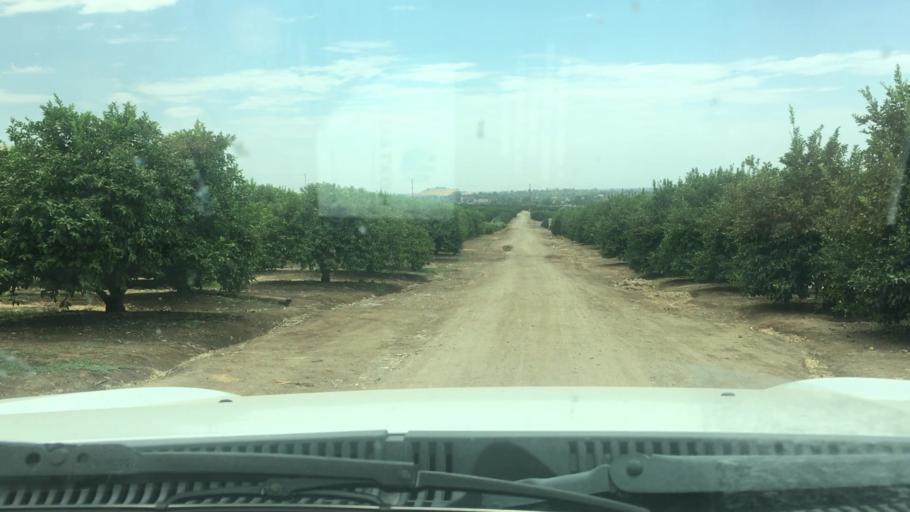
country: US
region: California
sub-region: Tulare County
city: Porterville
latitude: 36.0998
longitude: -119.0045
